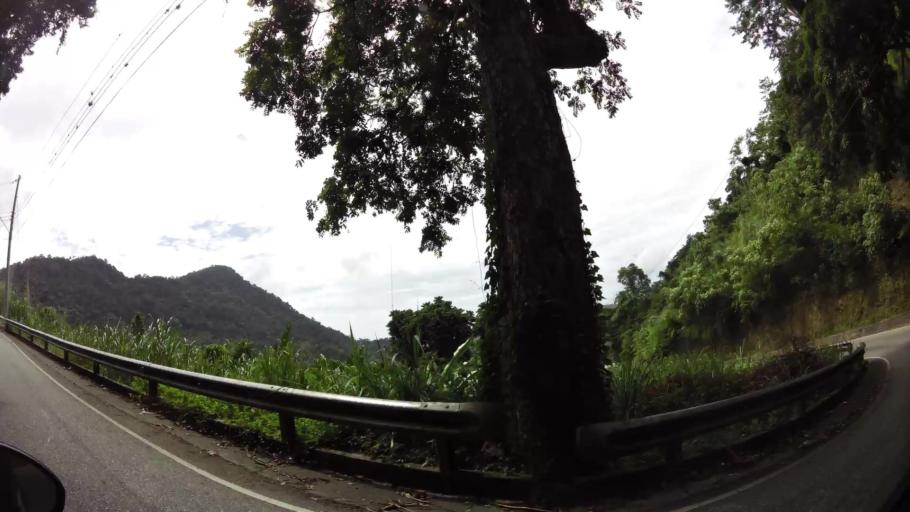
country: TT
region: Diego Martin
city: Petit Valley
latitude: 10.7168
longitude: -61.5294
